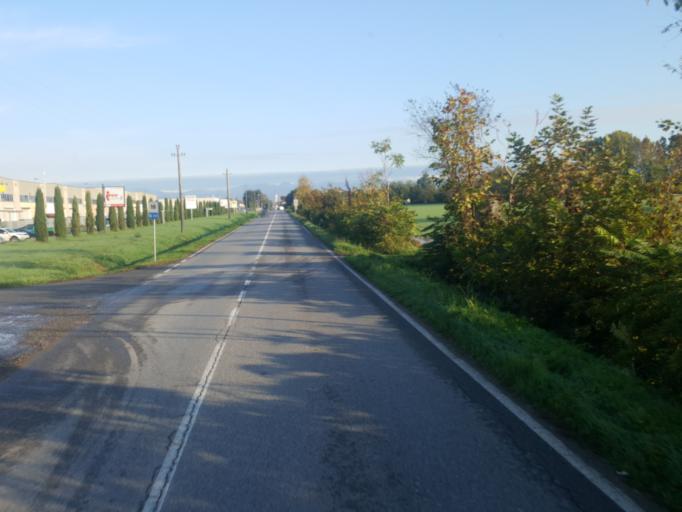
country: IT
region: Lombardy
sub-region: Provincia di Bergamo
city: Cologno al Serio
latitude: 45.5613
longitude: 9.7077
